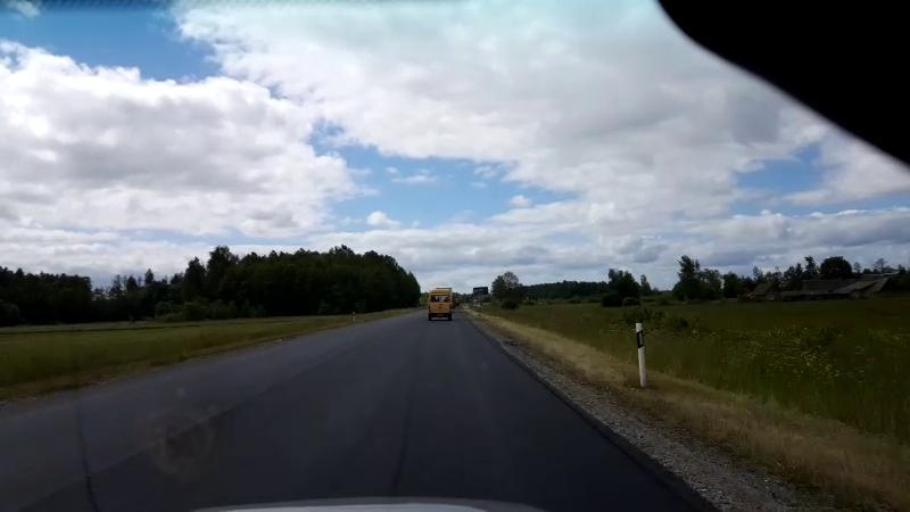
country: LV
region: Salacgrivas
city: Ainazi
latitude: 57.9020
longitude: 24.4123
